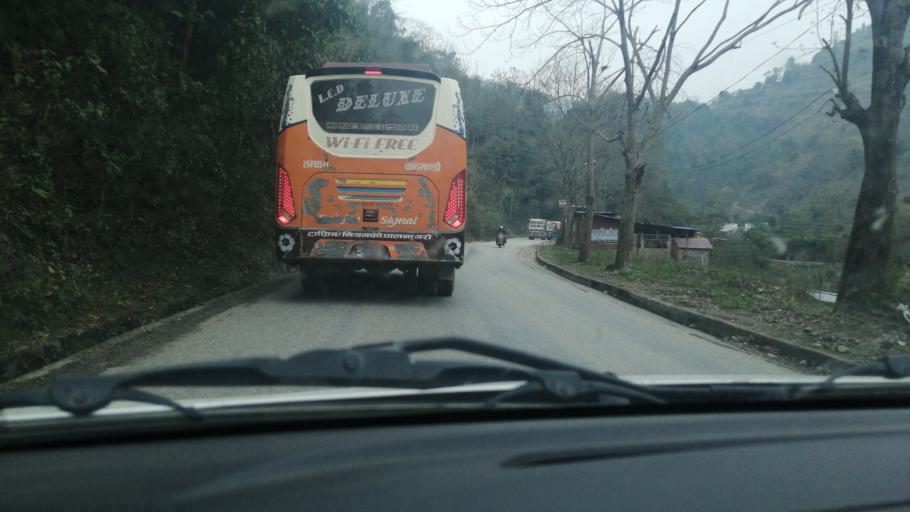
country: NP
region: Western Region
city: Tansen
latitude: 27.8094
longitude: 83.5197
